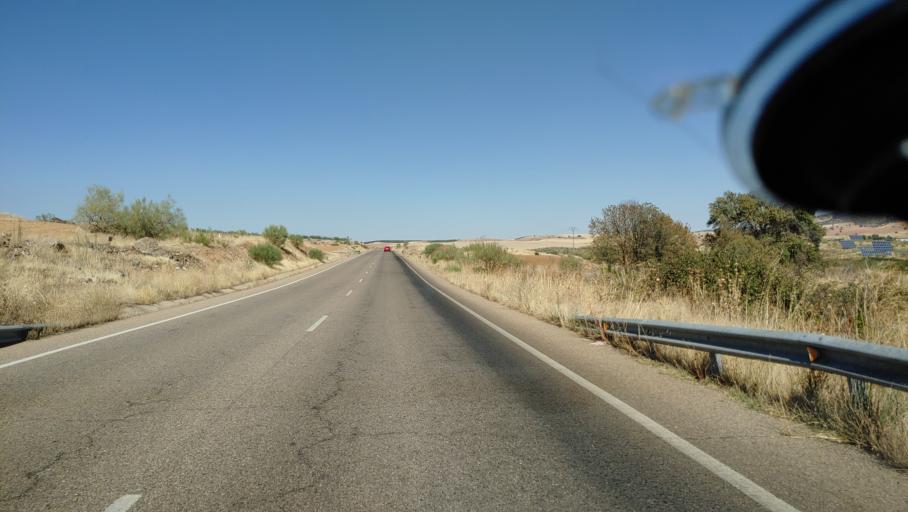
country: ES
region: Castille-La Mancha
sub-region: Province of Toledo
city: Casasbuenas
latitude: 39.7348
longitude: -4.1051
